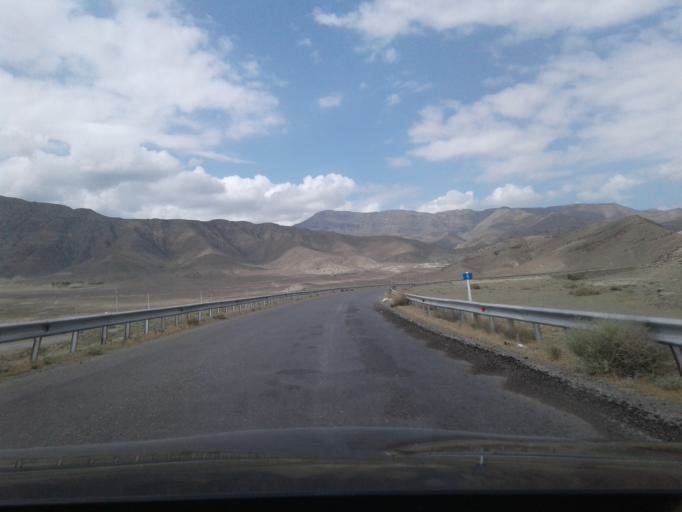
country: TM
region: Ahal
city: Baharly
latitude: 38.5024
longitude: 57.1224
